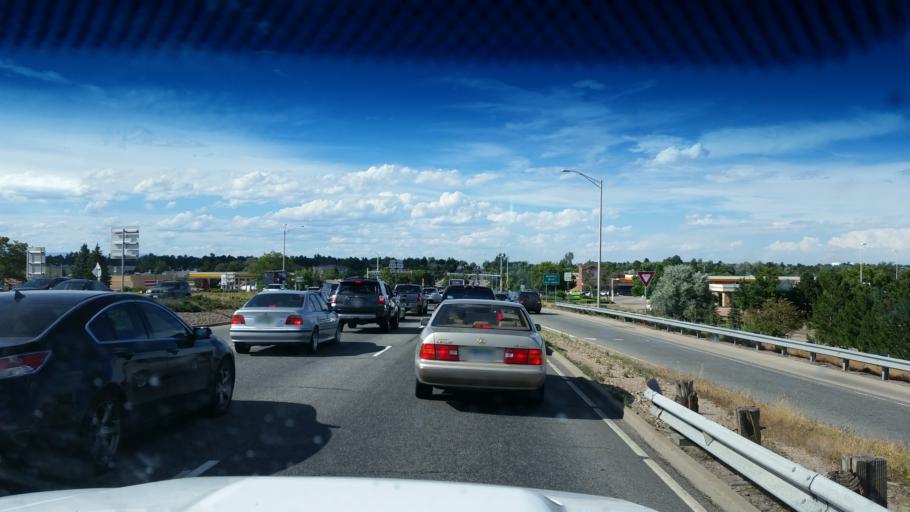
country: US
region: Colorado
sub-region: Broomfield County
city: Broomfield
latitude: 39.9202
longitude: -105.0906
